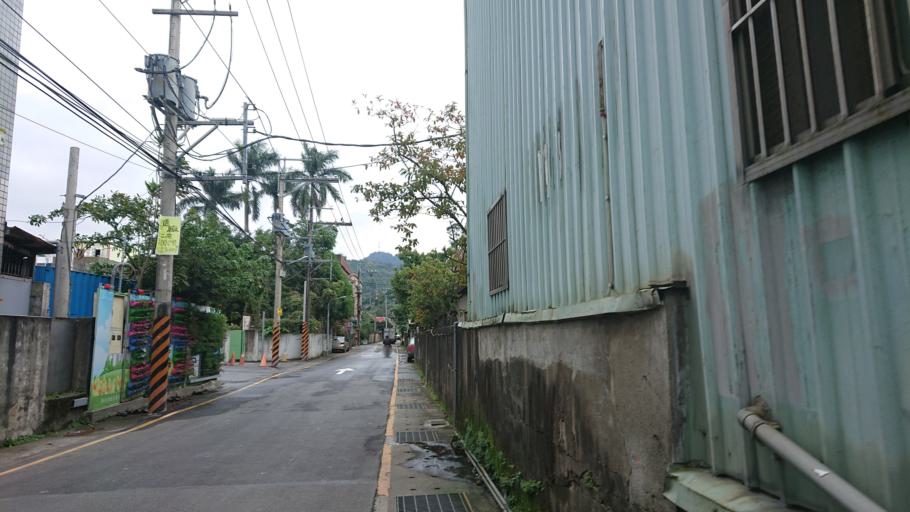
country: TW
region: Taipei
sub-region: Taipei
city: Banqiao
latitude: 24.9624
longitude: 121.4411
